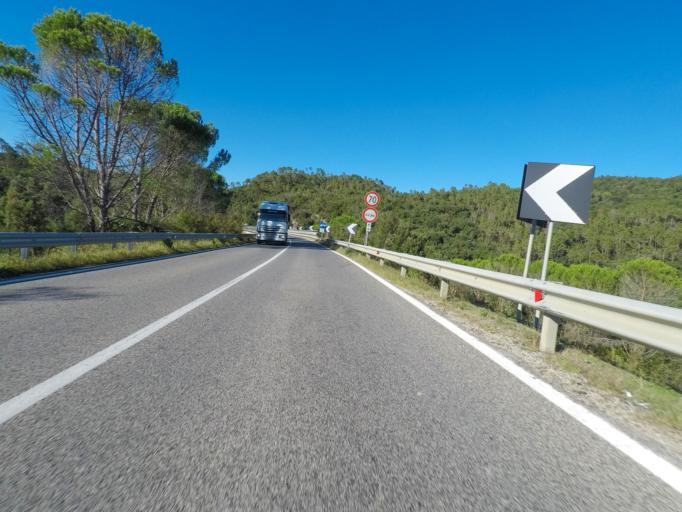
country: IT
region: Tuscany
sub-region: Provincia di Grosseto
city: Civitella Marittima
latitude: 43.0136
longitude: 11.2882
